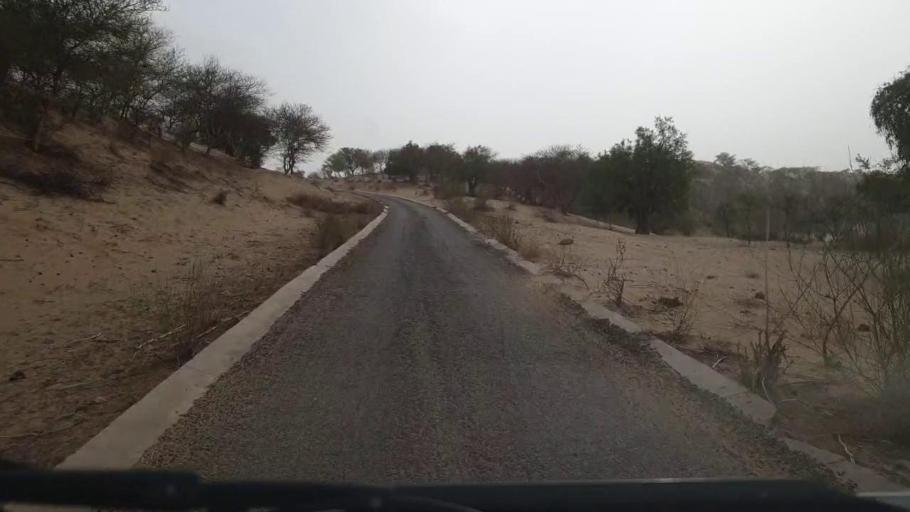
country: PK
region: Sindh
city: Islamkot
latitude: 25.0648
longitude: 70.5434
